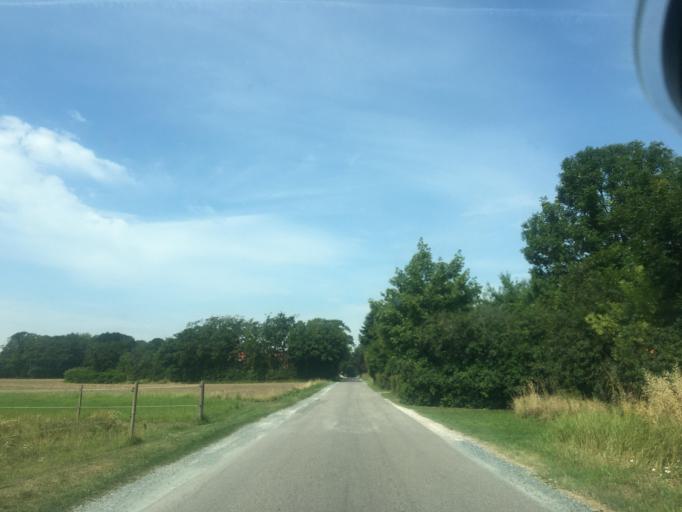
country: DK
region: Zealand
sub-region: Faxe Kommune
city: Fakse
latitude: 55.1816
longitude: 12.0895
